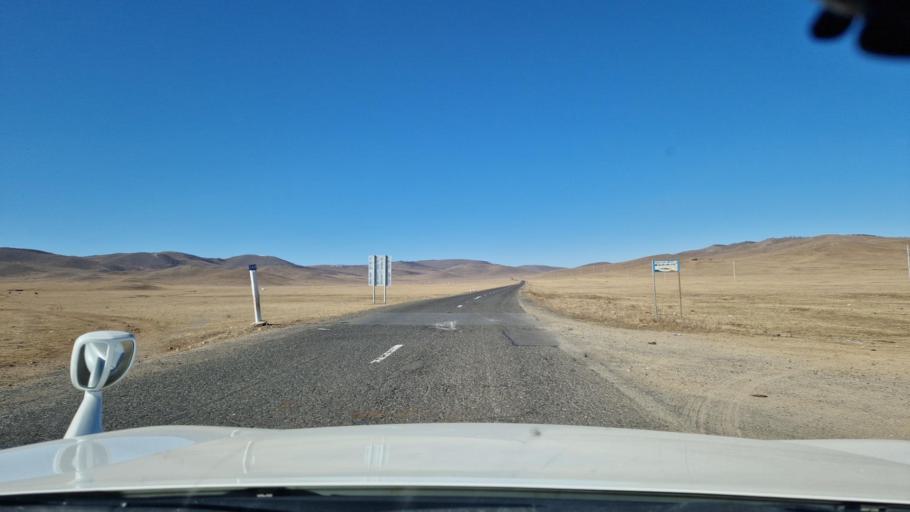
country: MN
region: Hentiy
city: Modot
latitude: 47.7627
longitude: 108.9145
